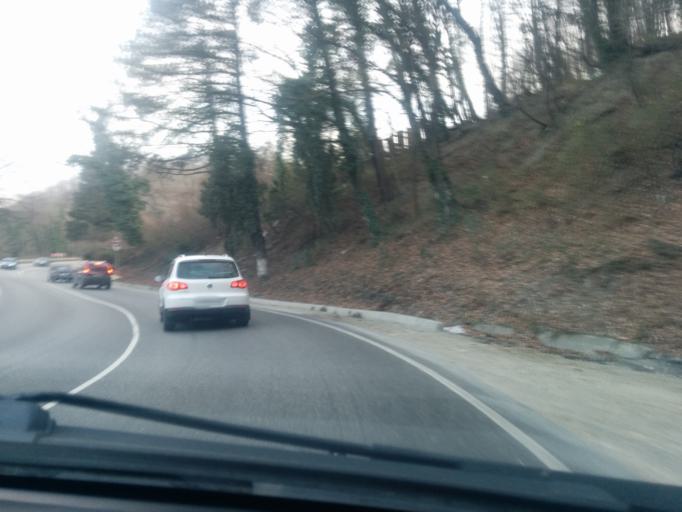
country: RU
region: Krasnodarskiy
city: Agoy
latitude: 44.1205
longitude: 39.0486
